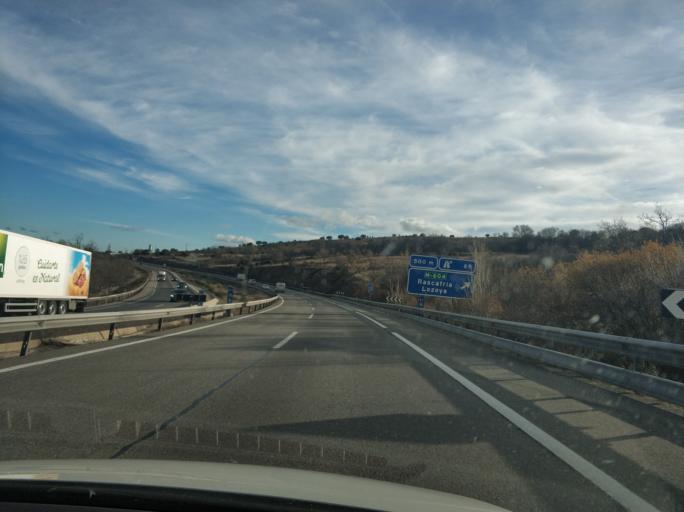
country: ES
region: Madrid
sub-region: Provincia de Madrid
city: Buitrago del Lozoya
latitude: 40.9476
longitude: -3.6393
